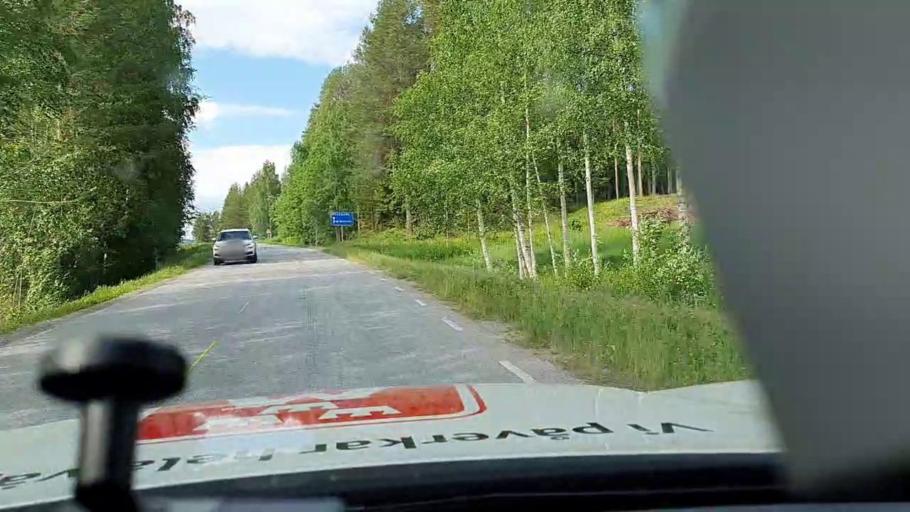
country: SE
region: Norrbotten
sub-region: Gallivare Kommun
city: Gaellivare
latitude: 66.4548
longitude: 20.6568
